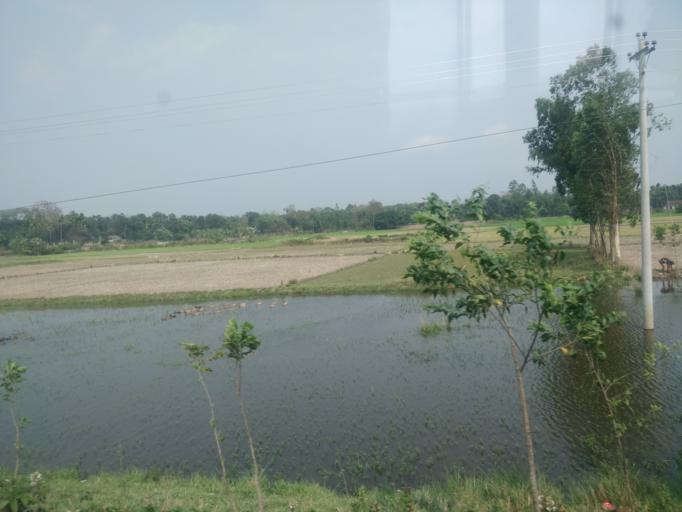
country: BD
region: Sylhet
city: Habiganj
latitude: 24.3210
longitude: 91.4347
